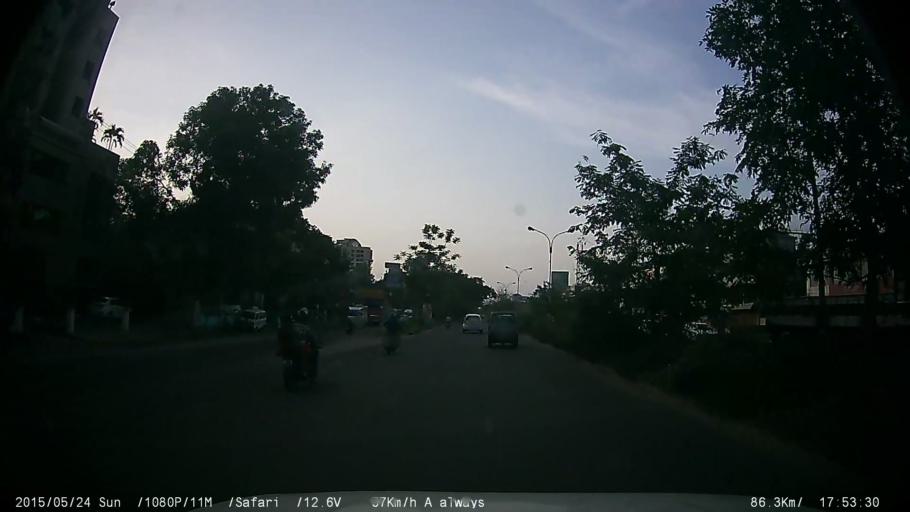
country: IN
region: Kerala
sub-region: Ernakulam
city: Elur
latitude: 10.0080
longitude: 76.3124
